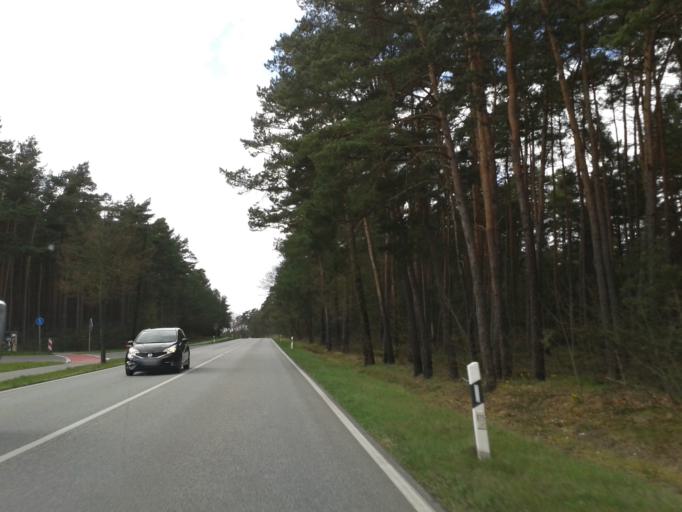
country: DE
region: Lower Saxony
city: Bergen an der Dumme
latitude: 52.8836
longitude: 11.0080
